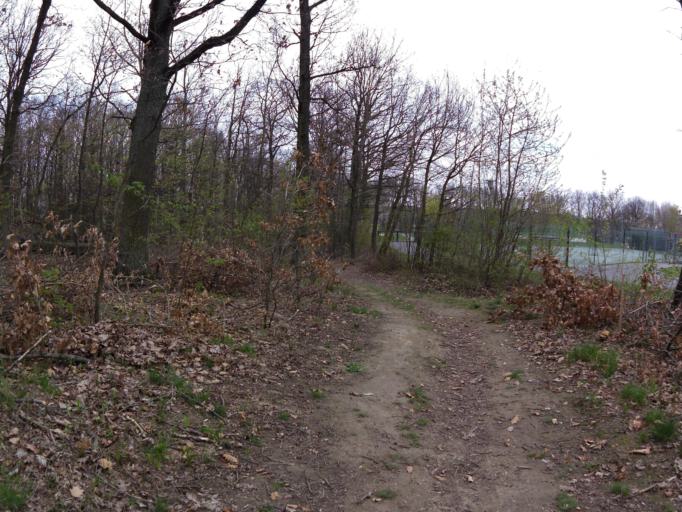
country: DE
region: Bavaria
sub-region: Regierungsbezirk Unterfranken
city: Rottendorf
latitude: 49.7982
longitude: 10.0172
